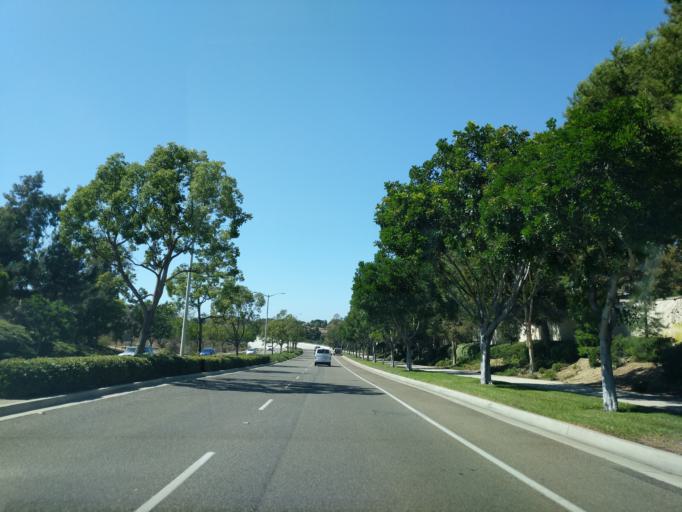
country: US
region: California
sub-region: Orange County
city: San Joaquin Hills
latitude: 33.6287
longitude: -117.8558
